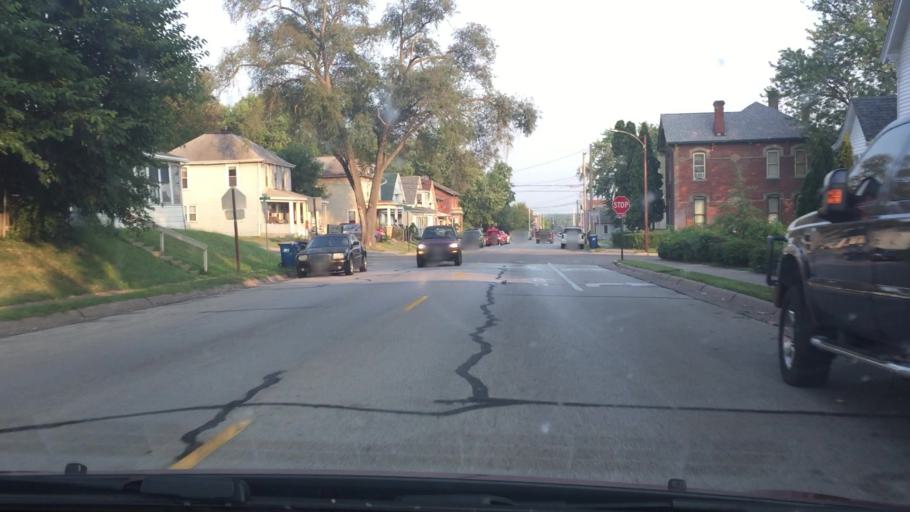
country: US
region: Iowa
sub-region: Muscatine County
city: Muscatine
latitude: 41.4288
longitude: -91.0466
